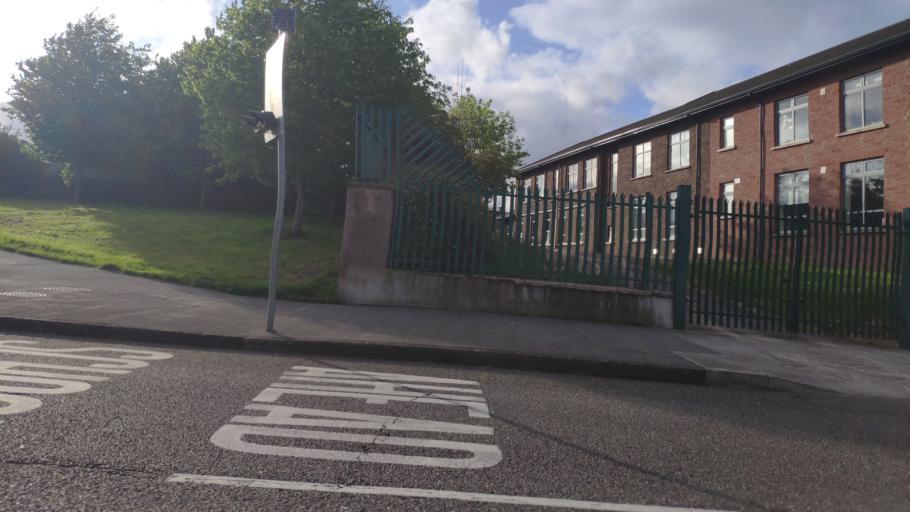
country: IE
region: Munster
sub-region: County Cork
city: Cork
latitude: 51.9102
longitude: -8.4848
